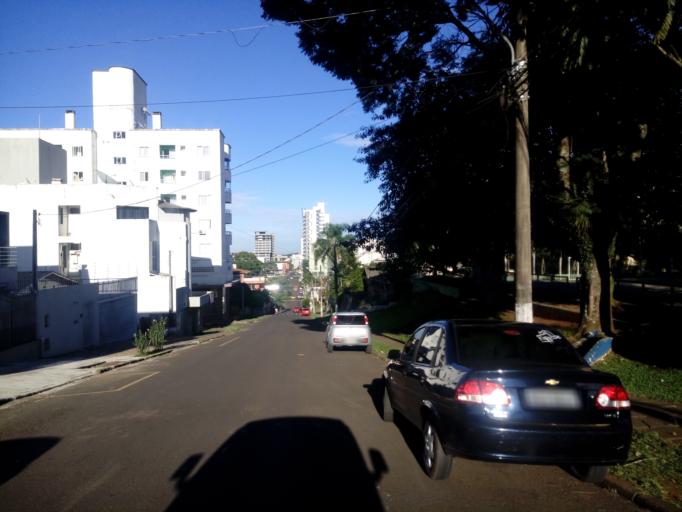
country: BR
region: Santa Catarina
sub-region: Chapeco
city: Chapeco
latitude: -27.0927
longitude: -52.6111
